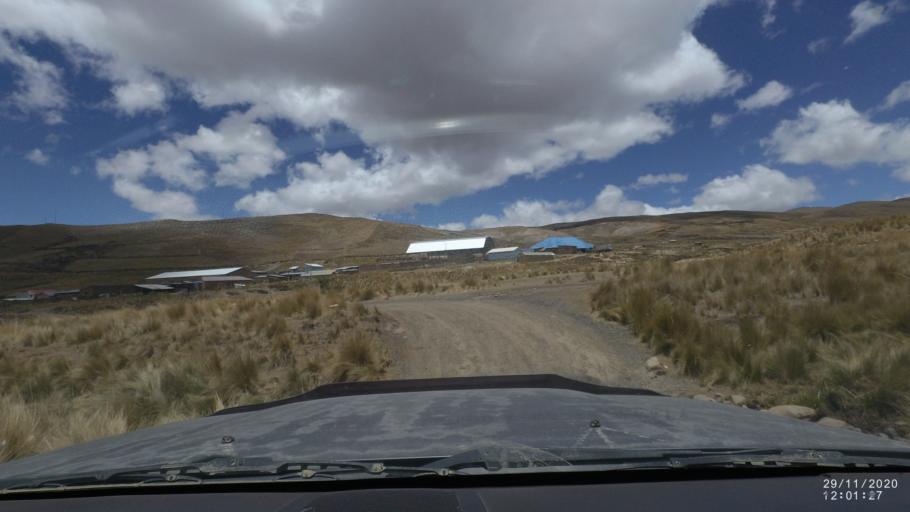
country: BO
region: Cochabamba
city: Cochabamba
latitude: -17.1511
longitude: -66.2813
